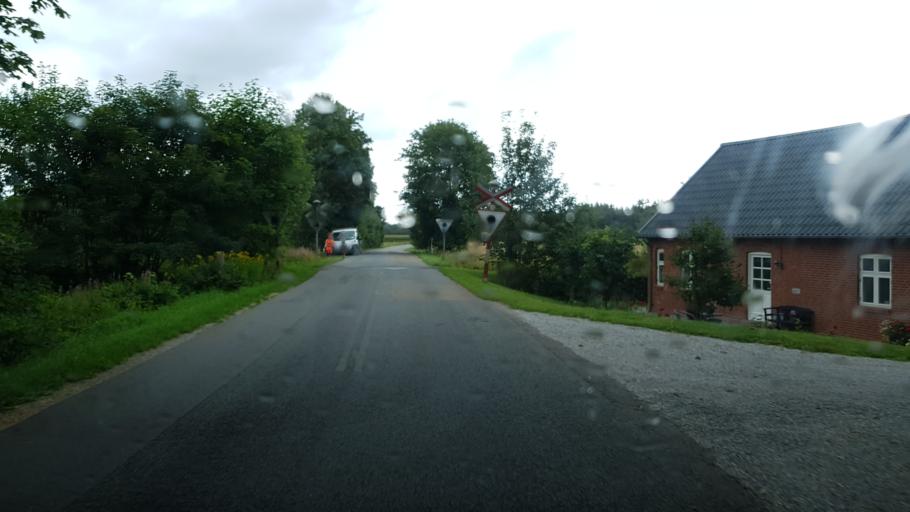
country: DK
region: South Denmark
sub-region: Billund Kommune
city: Grindsted
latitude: 55.6427
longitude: 8.8203
